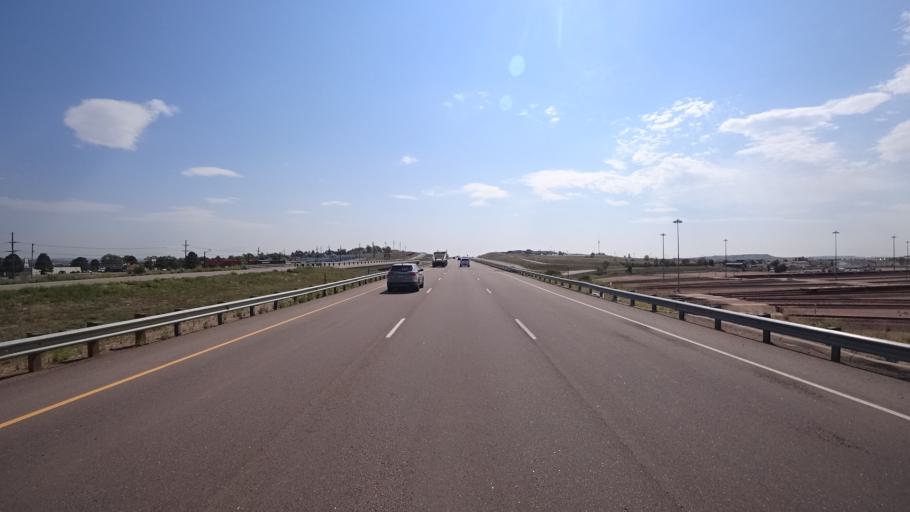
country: US
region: Colorado
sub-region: El Paso County
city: Stratmoor
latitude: 38.7657
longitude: -104.7989
